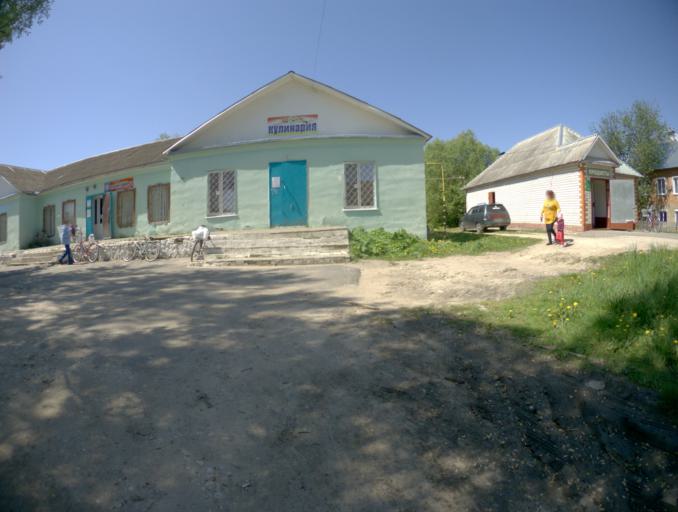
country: RU
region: Vladimir
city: Anopino
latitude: 55.6987
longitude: 40.6636
